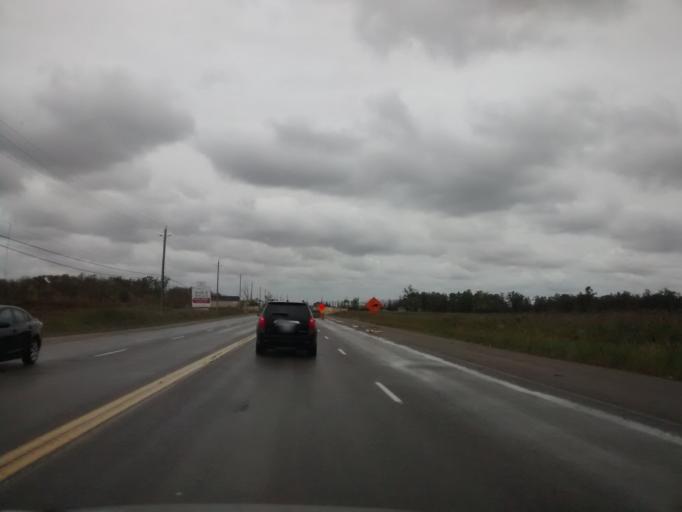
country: CA
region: Ontario
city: Hamilton
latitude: 43.1841
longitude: -79.7719
